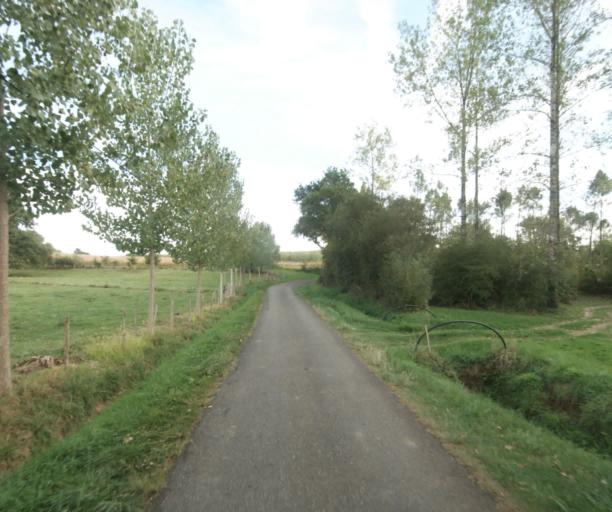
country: FR
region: Midi-Pyrenees
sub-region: Departement du Gers
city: Cazaubon
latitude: 43.8659
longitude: -0.1206
